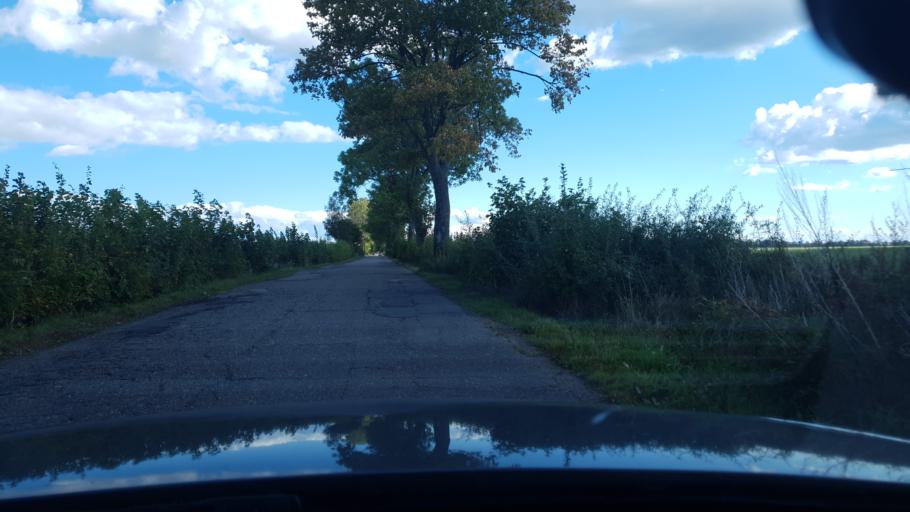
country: PL
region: Pomeranian Voivodeship
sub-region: Powiat pucki
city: Zelistrzewo
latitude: 54.6880
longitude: 18.4332
